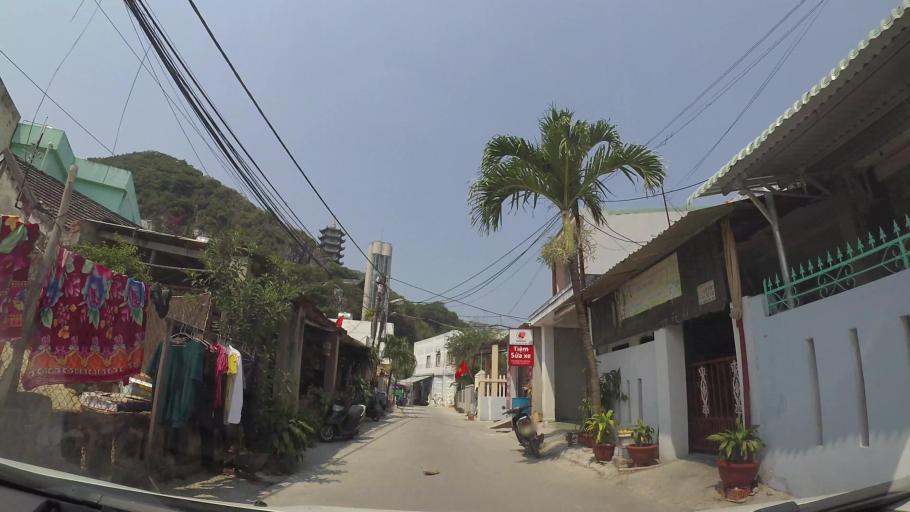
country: VN
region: Da Nang
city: Ngu Hanh Son
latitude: 16.0021
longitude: 108.2644
